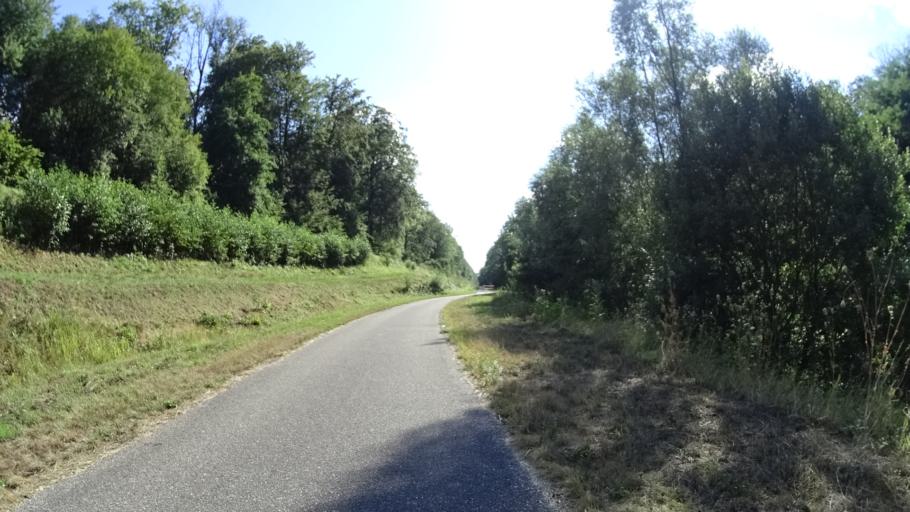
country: FR
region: Franche-Comte
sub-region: Territoire de Belfort
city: Montreux-Chateau
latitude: 47.6267
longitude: 7.0491
